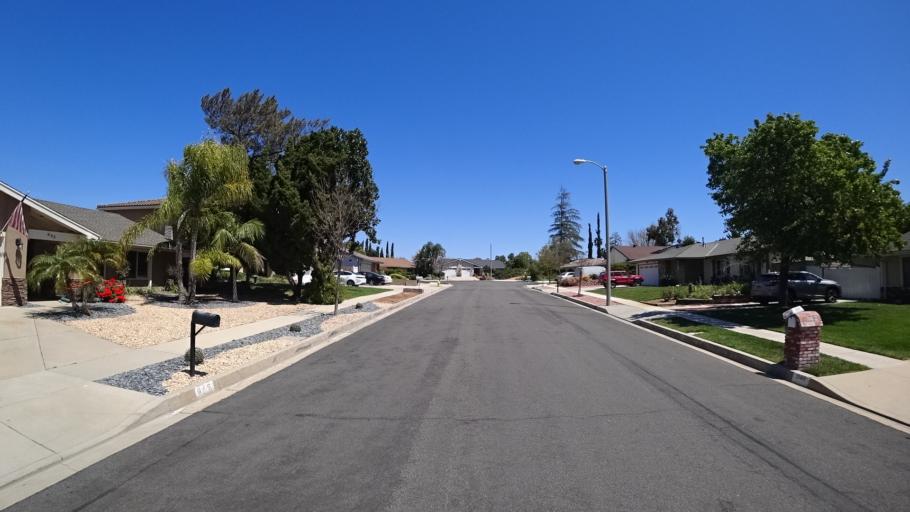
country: US
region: California
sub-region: Ventura County
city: Casa Conejo
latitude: 34.1801
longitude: -118.9017
